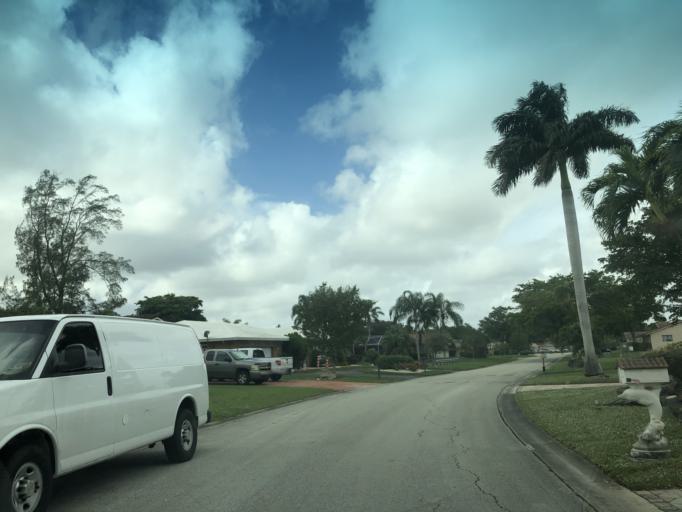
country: US
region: Florida
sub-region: Broward County
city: Margate
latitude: 26.2509
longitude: -80.2384
